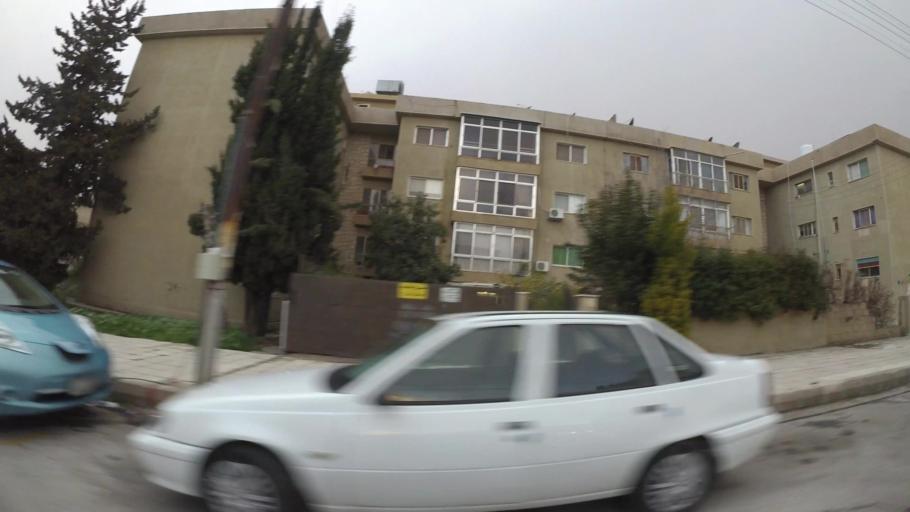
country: JO
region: Amman
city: Al Jubayhah
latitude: 31.9688
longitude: 35.8827
